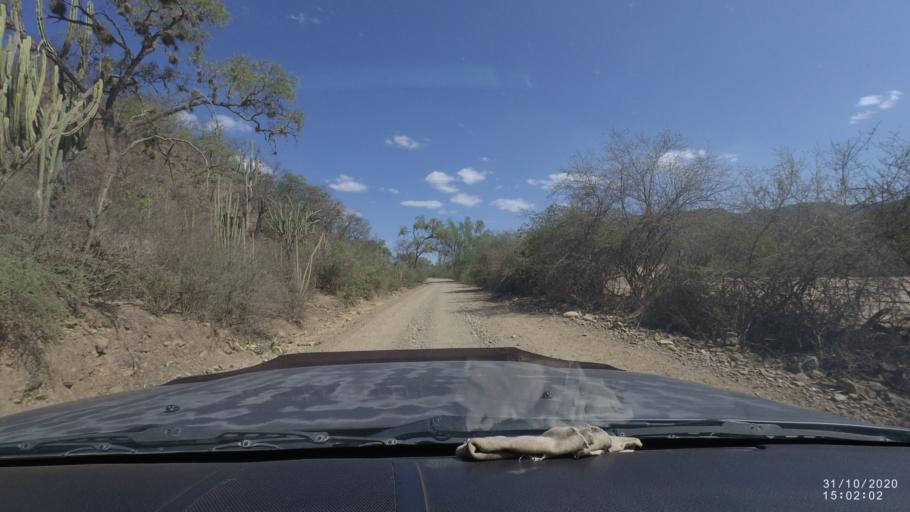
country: BO
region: Cochabamba
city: Aiquile
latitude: -18.2670
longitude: -64.8148
